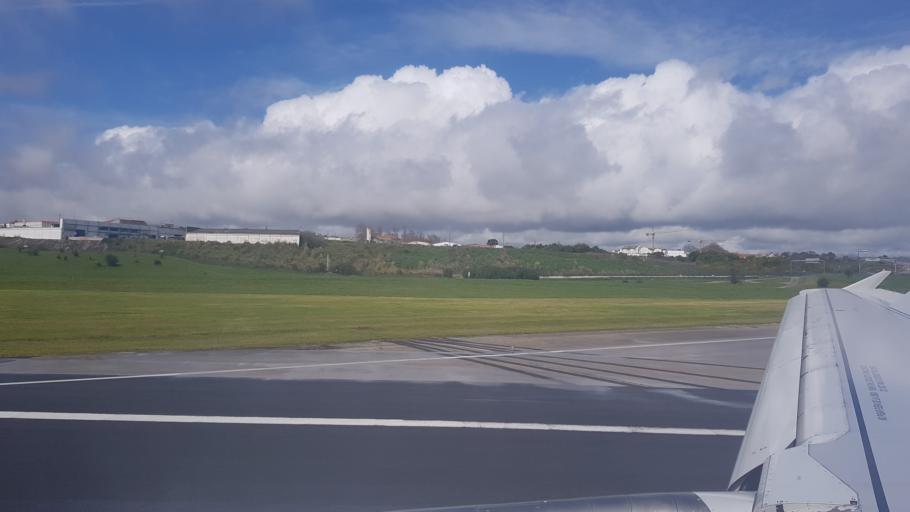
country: PT
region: Lisbon
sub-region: Loures
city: Camarate
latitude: 38.7816
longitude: -9.1358
